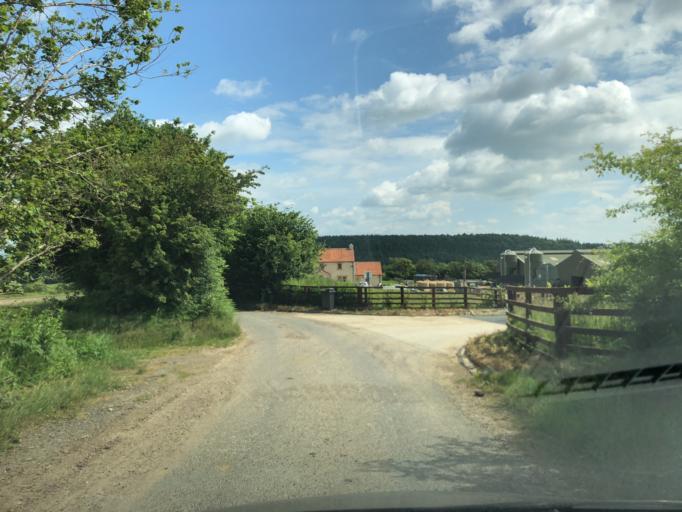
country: GB
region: England
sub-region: North Yorkshire
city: Helmsley
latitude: 54.1542
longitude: -1.0052
